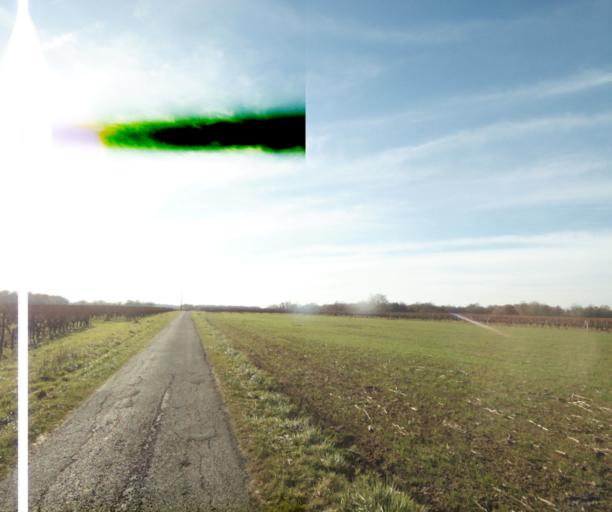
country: FR
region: Poitou-Charentes
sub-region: Departement de la Charente-Maritime
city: Burie
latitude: 45.7803
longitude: -0.4474
